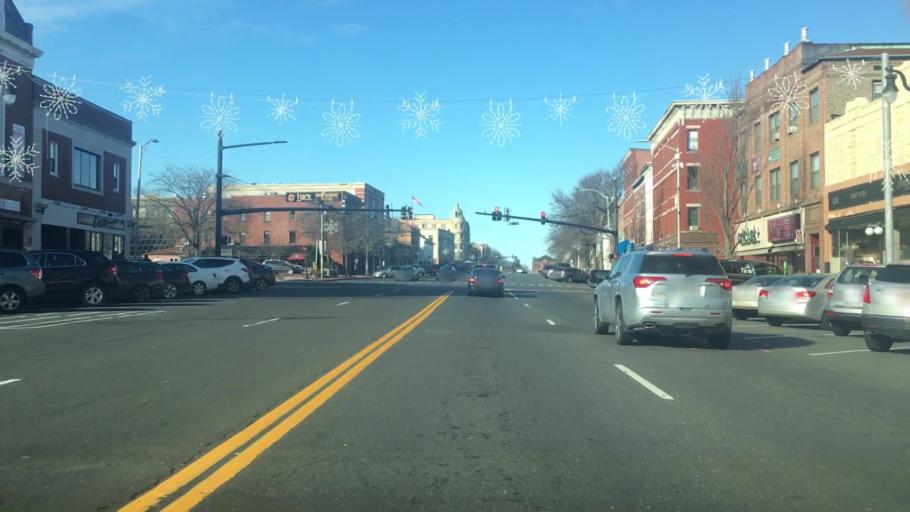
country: US
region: Connecticut
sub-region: Middlesex County
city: Middletown
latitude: 41.5618
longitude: -72.6506
